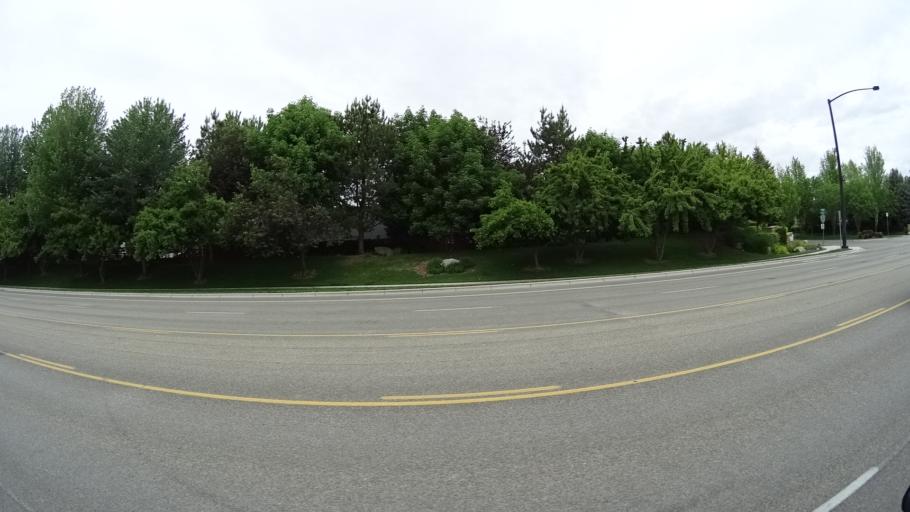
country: US
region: Idaho
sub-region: Ada County
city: Meridian
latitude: 43.6338
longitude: -116.3652
